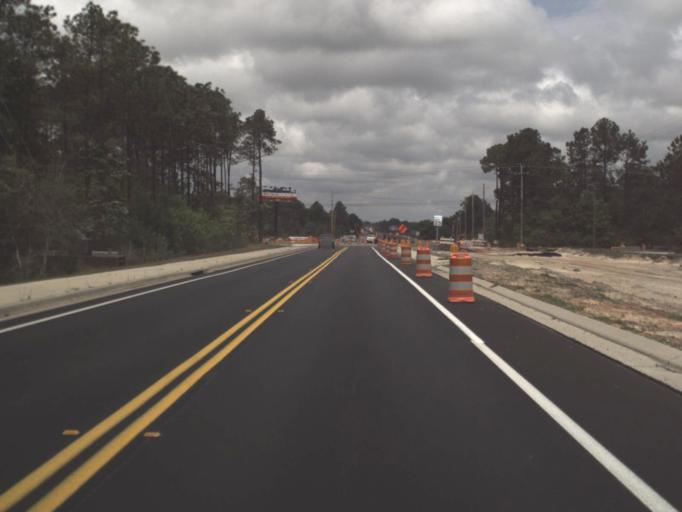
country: US
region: Florida
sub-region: Santa Rosa County
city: Bagdad
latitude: 30.5429
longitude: -87.0874
